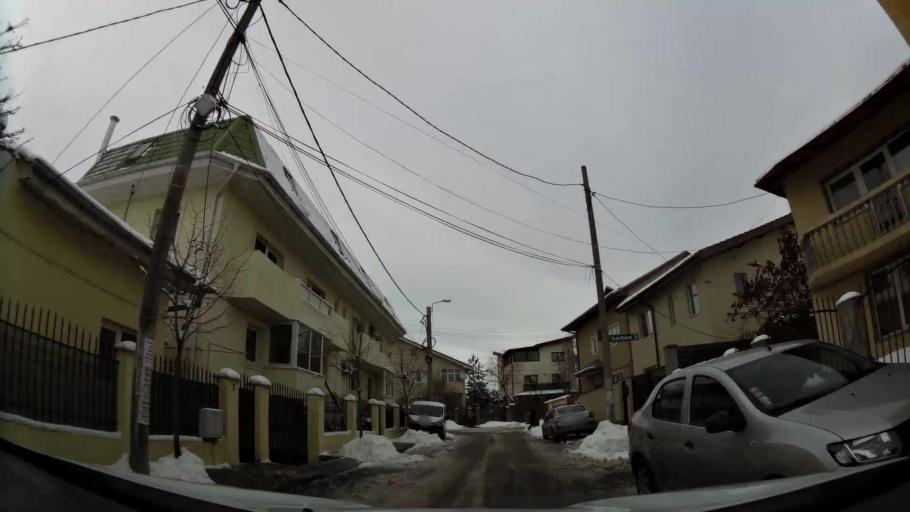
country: RO
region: Bucuresti
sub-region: Municipiul Bucuresti
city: Bucuresti
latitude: 44.3907
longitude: 26.1017
